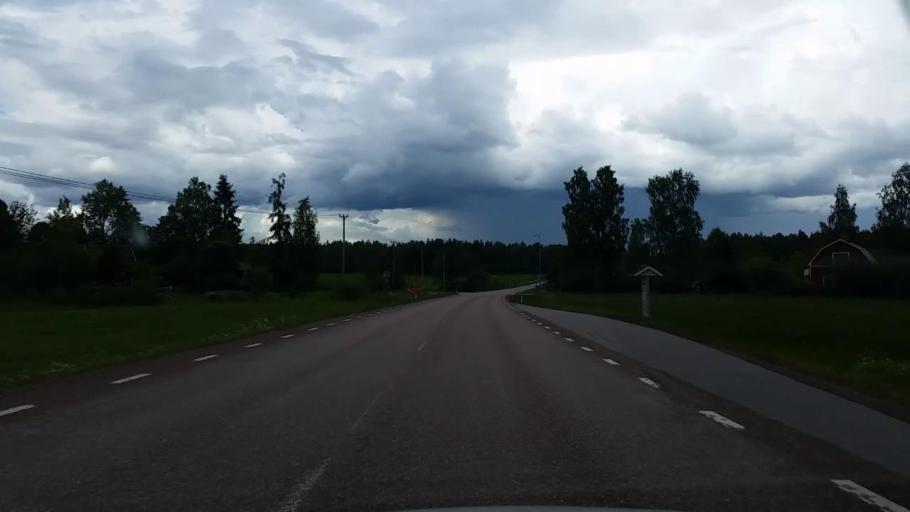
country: SE
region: Gaevleborg
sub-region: Hofors Kommun
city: Hofors
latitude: 60.5142
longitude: 16.4360
